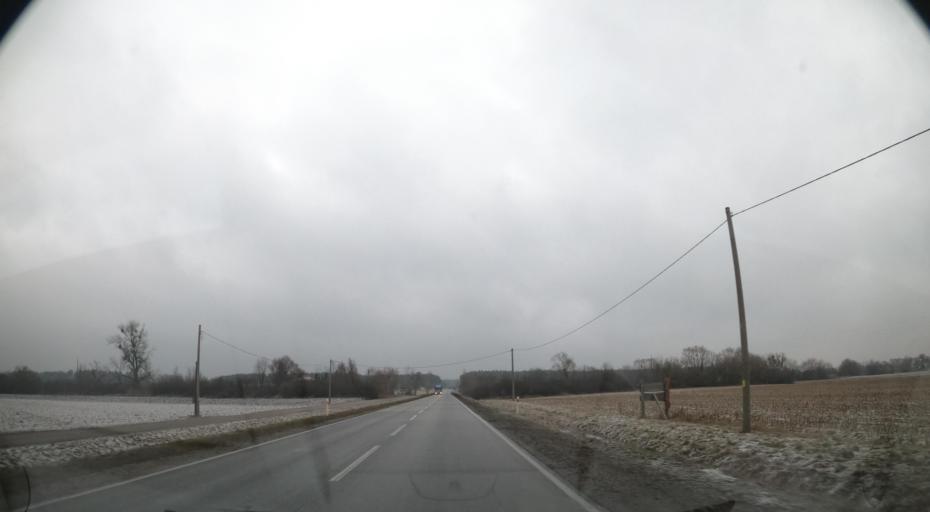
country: PL
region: Masovian Voivodeship
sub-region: Powiat sochaczewski
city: Mlodzieszyn
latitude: 52.3016
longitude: 20.1873
